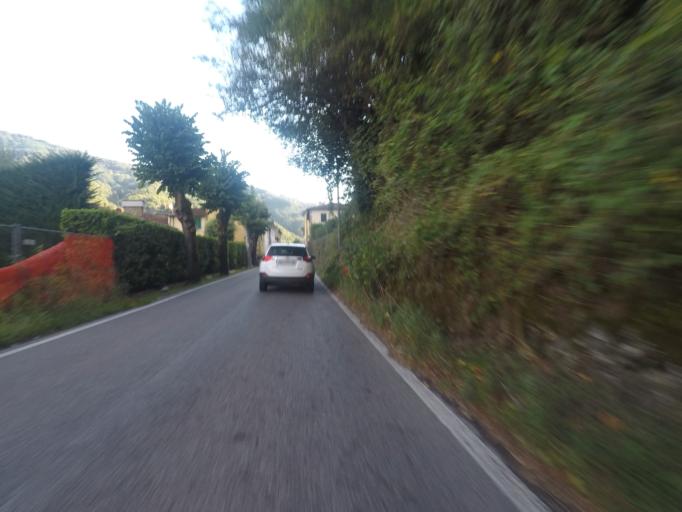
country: IT
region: Tuscany
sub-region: Provincia di Lucca
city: Bagni di Lucca
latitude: 44.0034
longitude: 10.5617
